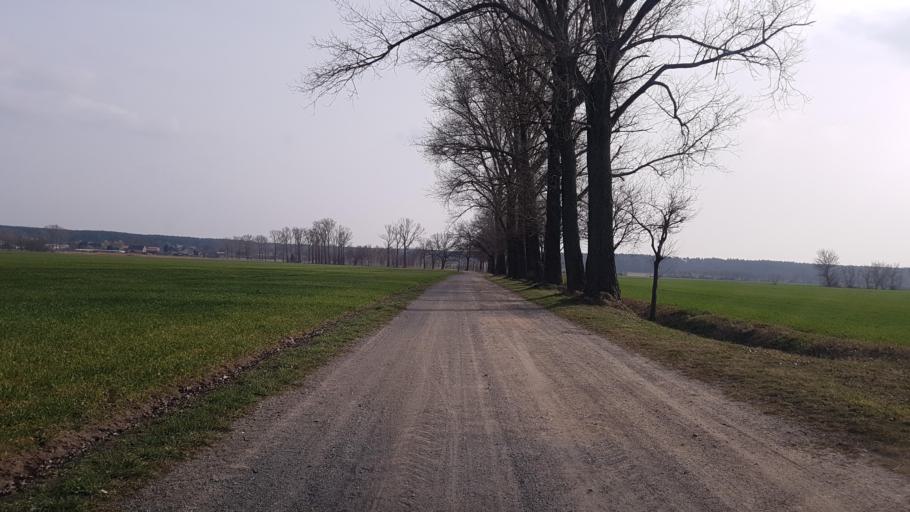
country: DE
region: Brandenburg
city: Merzdorf
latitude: 51.4149
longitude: 13.5266
